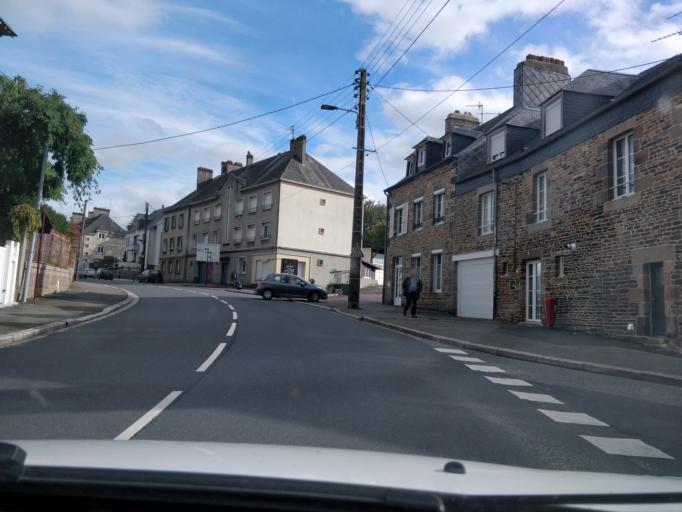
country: FR
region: Lower Normandy
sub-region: Departement du Calvados
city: Vire
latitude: 48.8404
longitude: -0.8956
